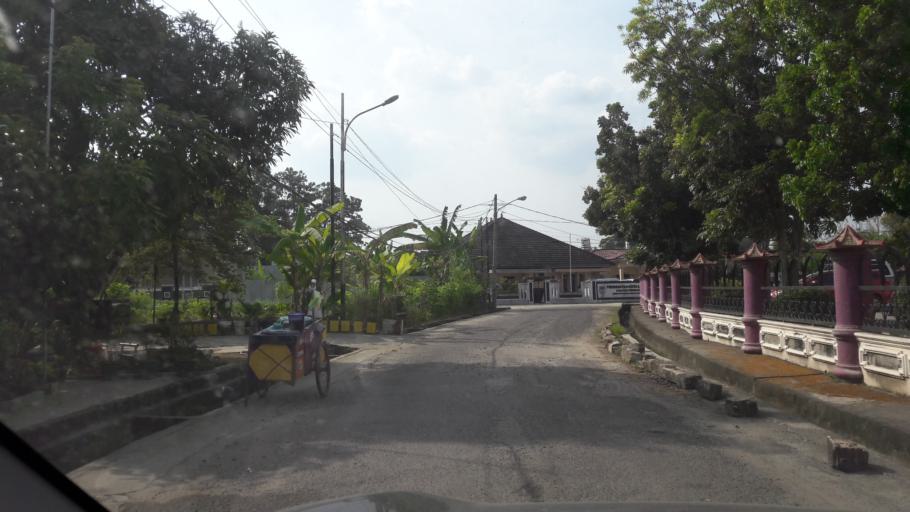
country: ID
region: South Sumatra
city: Plaju
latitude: -3.0245
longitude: 104.7797
